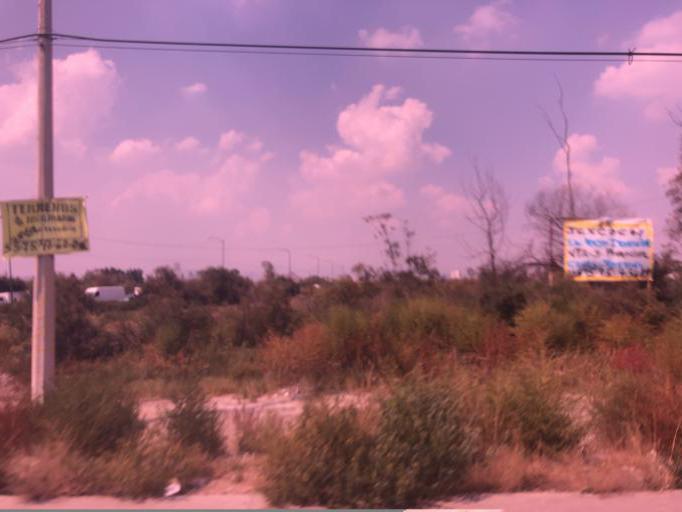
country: MX
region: Mexico
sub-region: Ciudad Nezahualcoyotl
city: Colonia Gustavo Baz Prada
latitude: 19.4572
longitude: -99.0384
